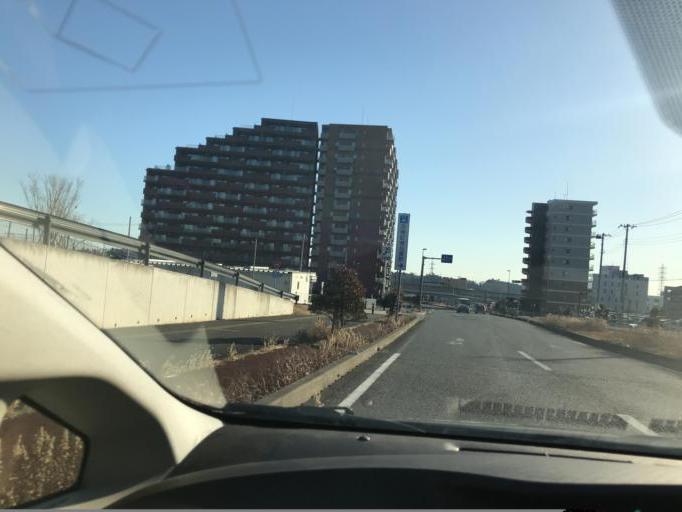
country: JP
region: Ibaraki
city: Mitsukaido
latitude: 36.0598
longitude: 140.0557
